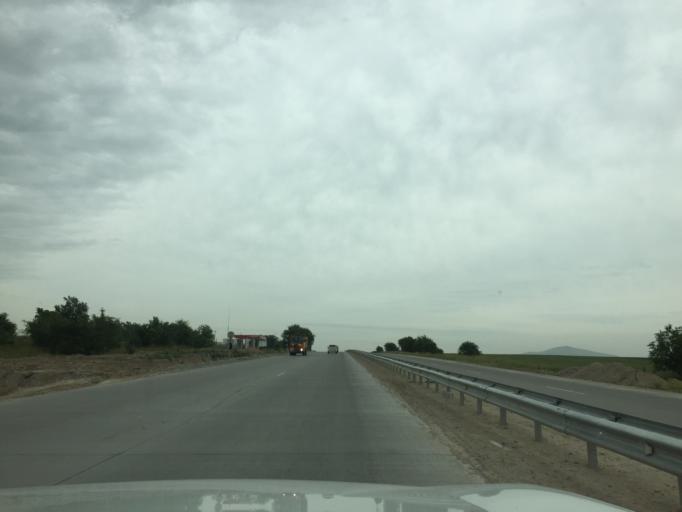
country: KZ
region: Ongtustik Qazaqstan
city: Aksu
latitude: 42.4741
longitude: 69.9022
